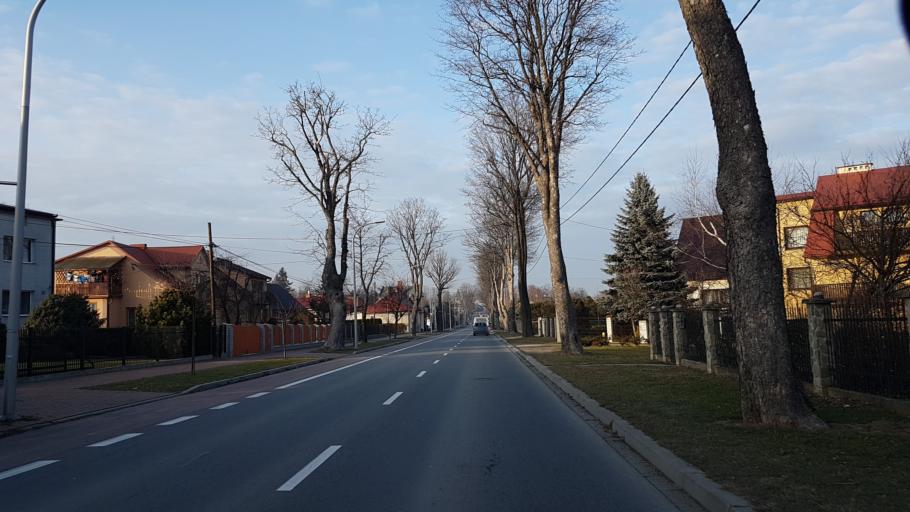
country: PL
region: Lesser Poland Voivodeship
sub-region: Powiat nowosadecki
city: Stary Sacz
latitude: 49.5524
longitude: 20.6399
